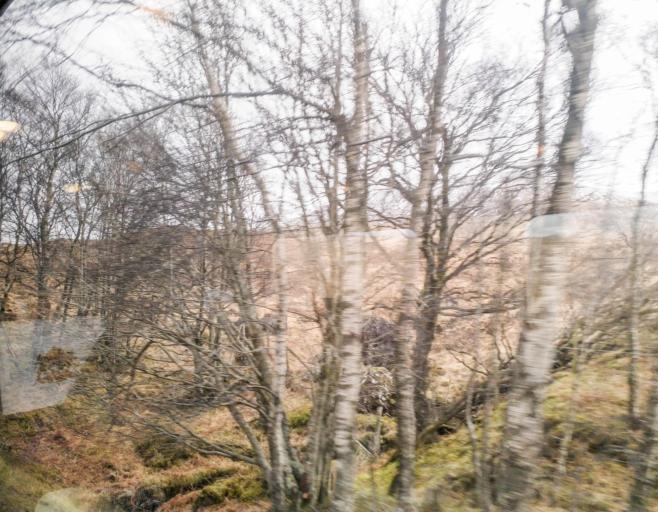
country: GB
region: Scotland
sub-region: Highland
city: Spean Bridge
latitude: 56.5841
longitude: -4.6691
